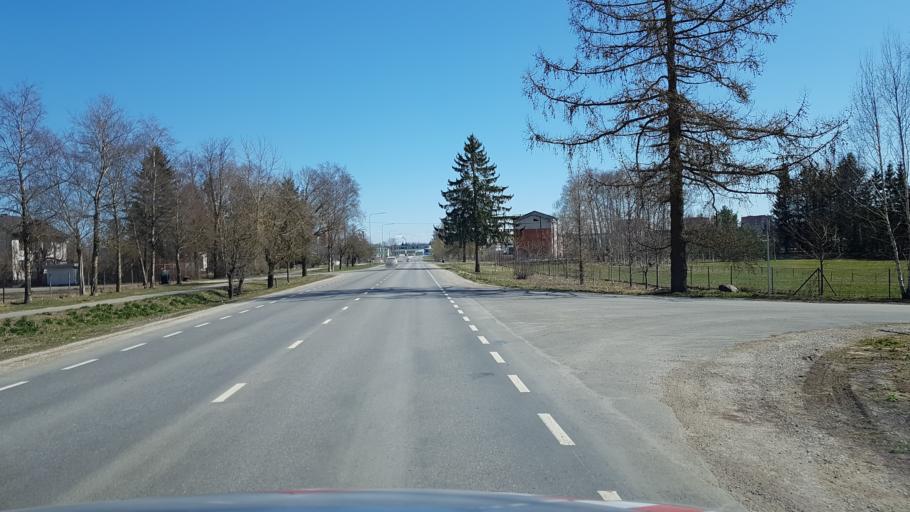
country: EE
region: Ida-Virumaa
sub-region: Johvi vald
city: Johvi
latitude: 59.3518
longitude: 27.4009
